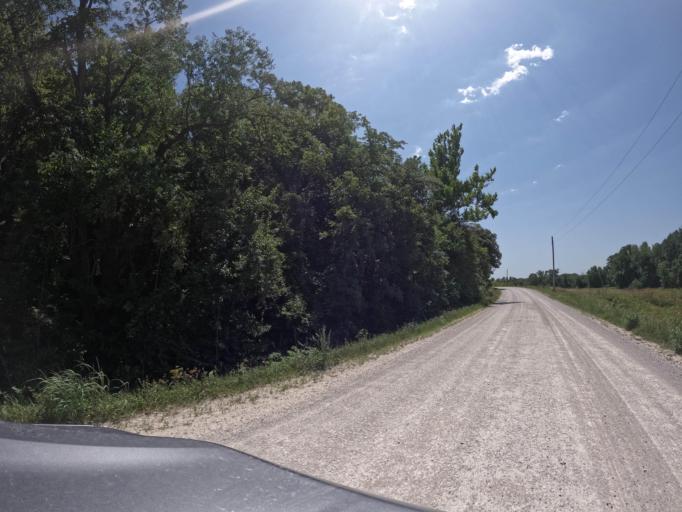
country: US
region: Iowa
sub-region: Henry County
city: Mount Pleasant
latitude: 40.9000
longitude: -91.5515
